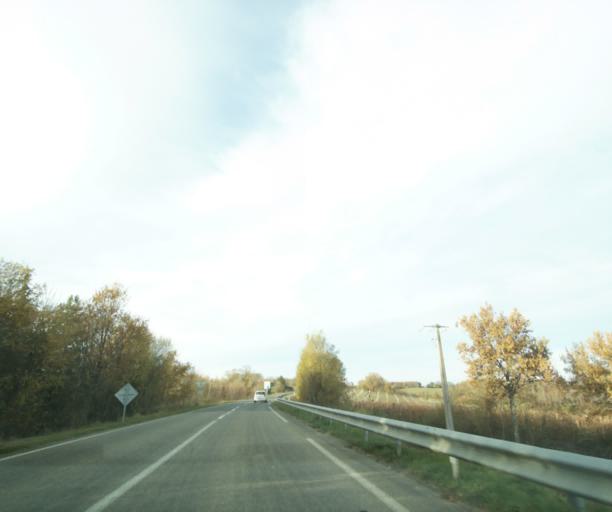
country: FR
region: Midi-Pyrenees
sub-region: Departement du Gers
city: Eauze
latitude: 43.7935
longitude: 0.1008
